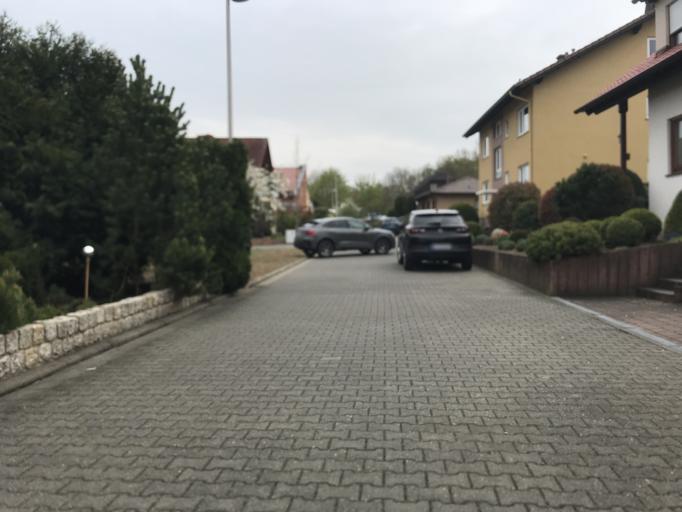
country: DE
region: Rheinland-Pfalz
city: Gau-Algesheim
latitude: 49.9493
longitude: 8.0149
